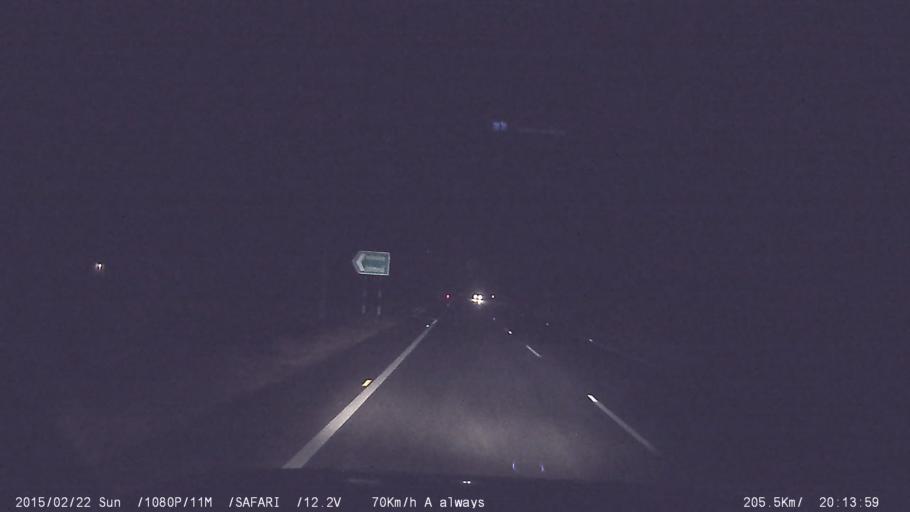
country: IN
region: Tamil Nadu
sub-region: Dindigul
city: Nilakottai
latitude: 10.2510
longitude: 77.8297
